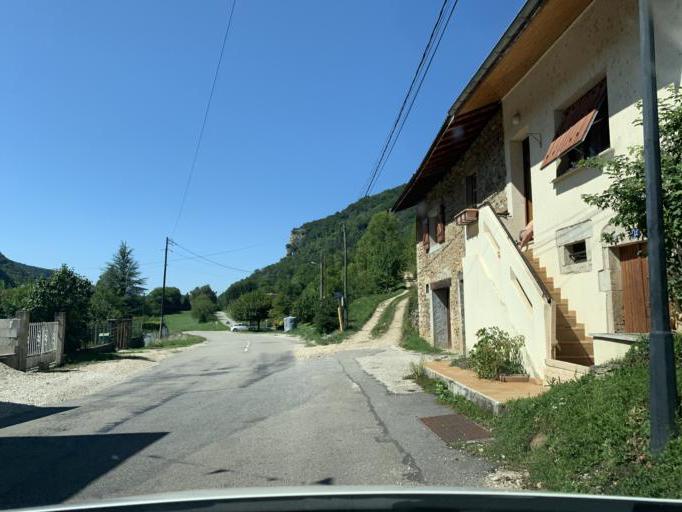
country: FR
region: Rhone-Alpes
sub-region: Departement de l'Ain
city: Vaux-en-Bugey
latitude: 45.9252
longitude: 5.3943
